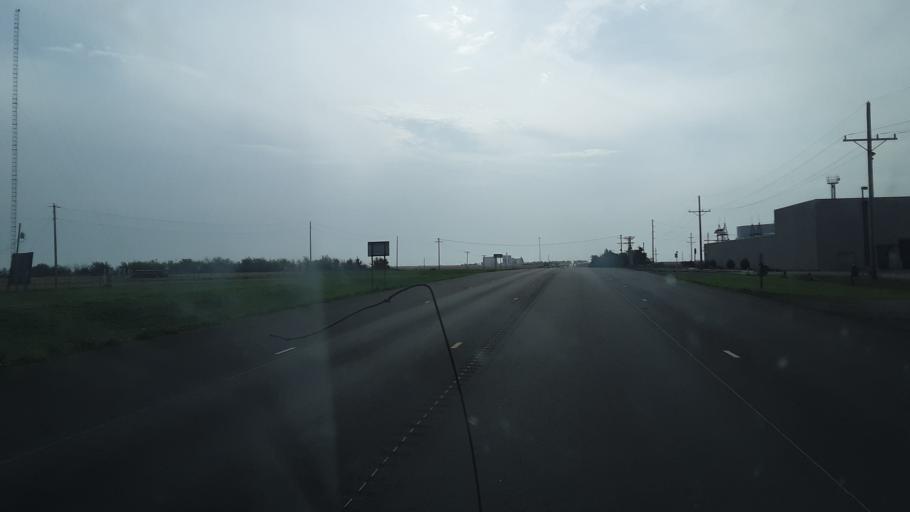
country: US
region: Kansas
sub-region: Ford County
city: Dodge City
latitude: 37.7791
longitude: -99.9316
